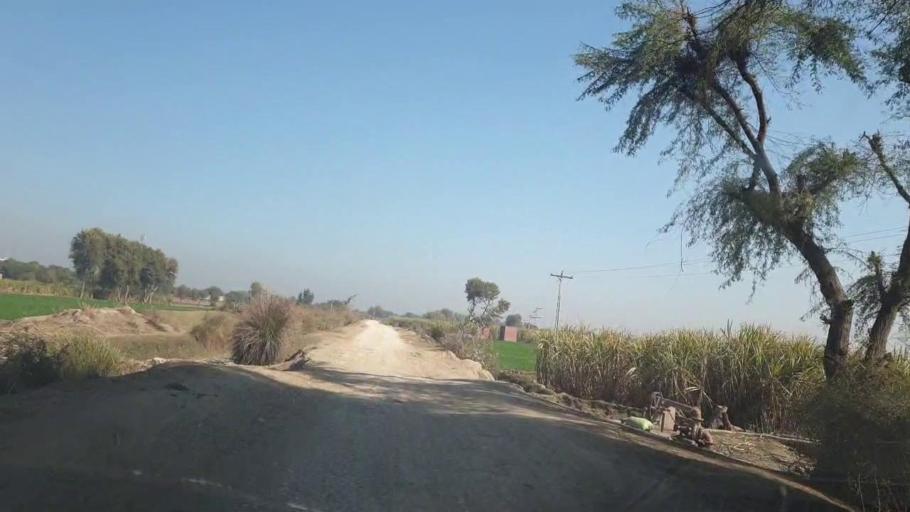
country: PK
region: Sindh
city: Mirpur Mathelo
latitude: 28.1252
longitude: 69.4952
